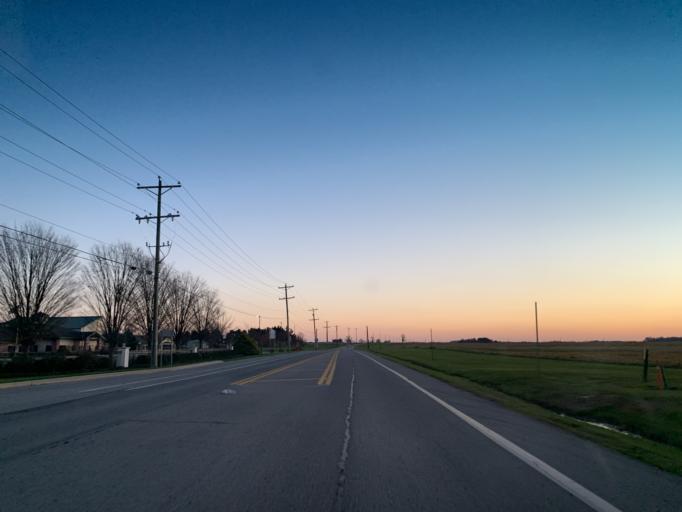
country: US
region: Delaware
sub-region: New Castle County
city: Middletown
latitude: 39.4239
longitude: -75.7408
